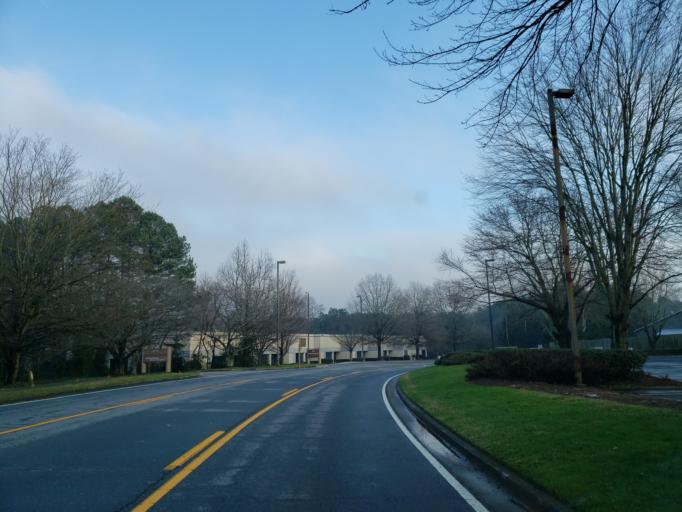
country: US
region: Georgia
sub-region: Cobb County
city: Kennesaw
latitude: 34.0058
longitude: -84.5946
